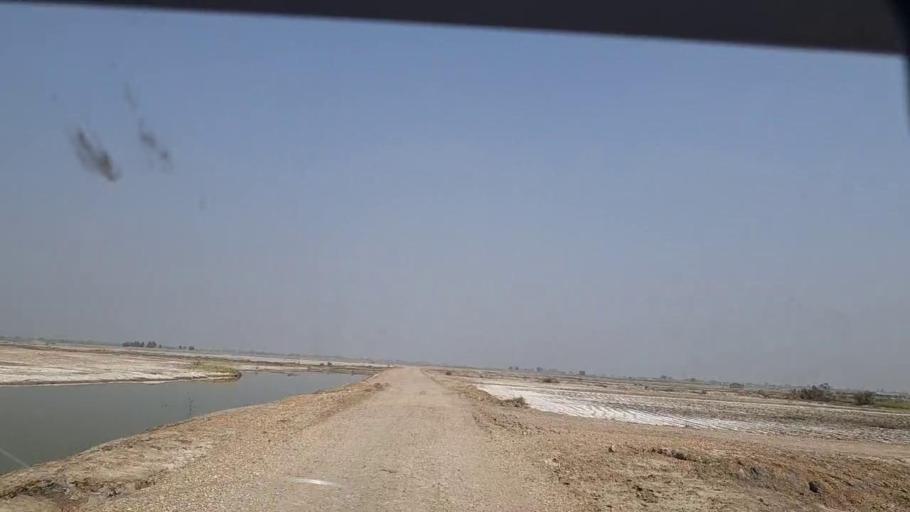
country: PK
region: Sindh
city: Shikarpur
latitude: 28.0495
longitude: 68.6553
